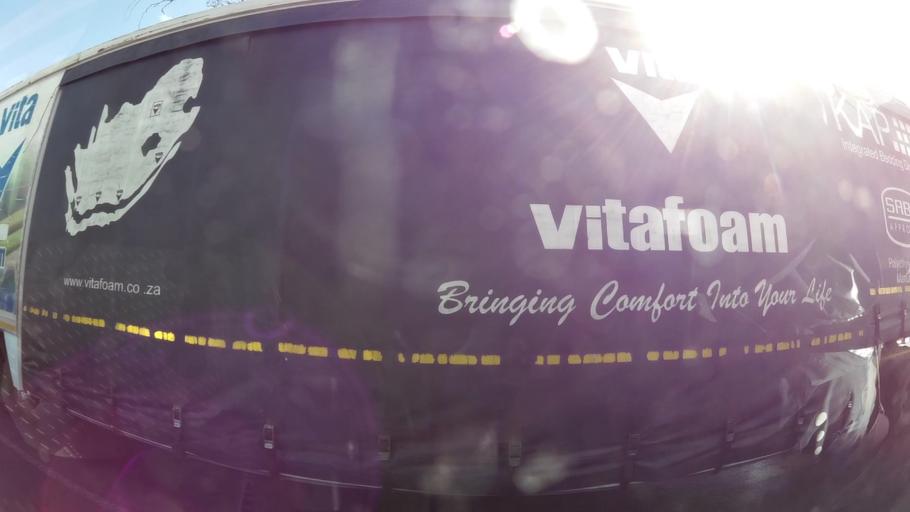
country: ZA
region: Gauteng
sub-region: West Rand District Municipality
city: Krugersdorp
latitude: -26.0909
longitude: 27.7802
